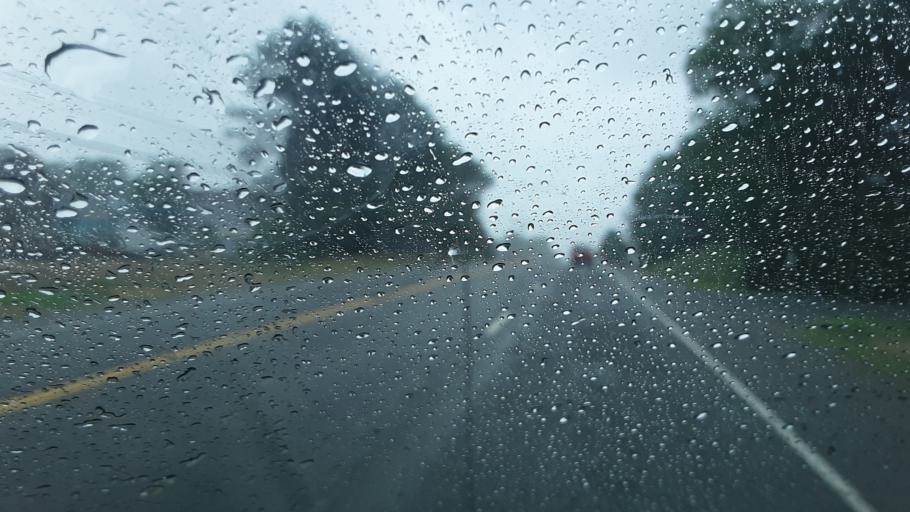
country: US
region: Maine
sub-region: Penobscot County
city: Millinocket
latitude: 45.6574
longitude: -68.6940
